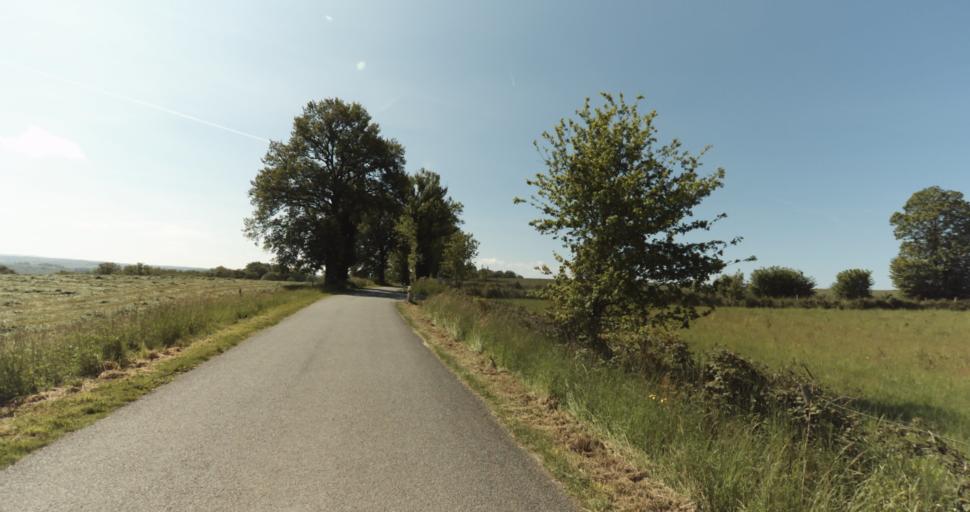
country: FR
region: Limousin
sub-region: Departement de la Haute-Vienne
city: Le Vigen
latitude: 45.7203
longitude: 1.2875
